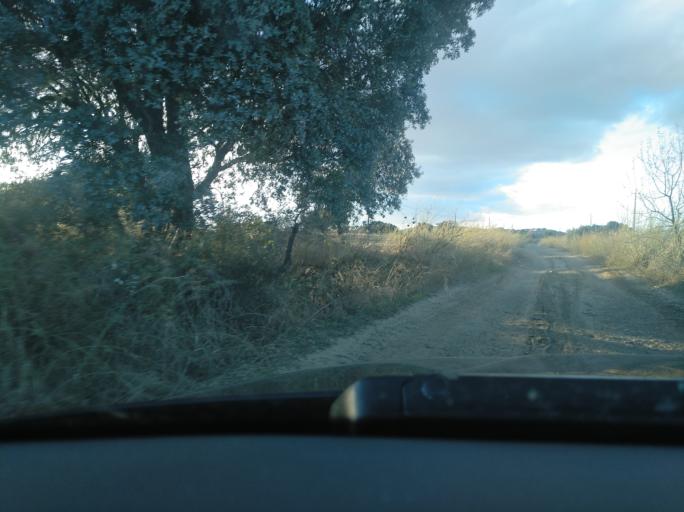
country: PT
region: Portalegre
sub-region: Campo Maior
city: Campo Maior
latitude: 39.0362
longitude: -6.9873
